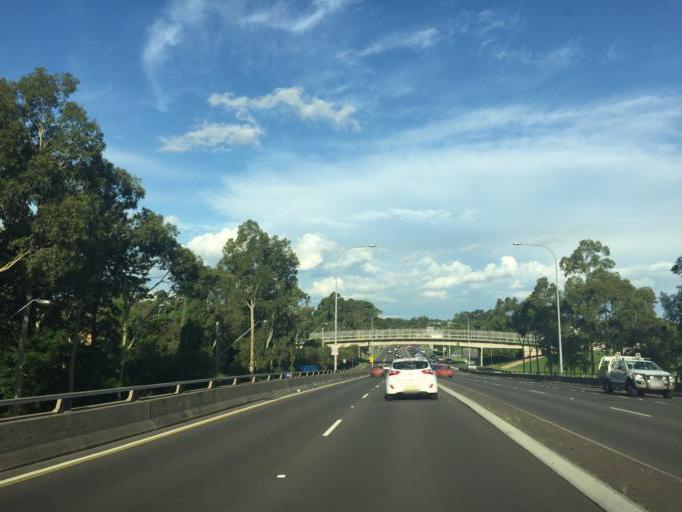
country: AU
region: New South Wales
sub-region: Parramatta
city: Harris Park
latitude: -33.8092
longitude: 151.0240
